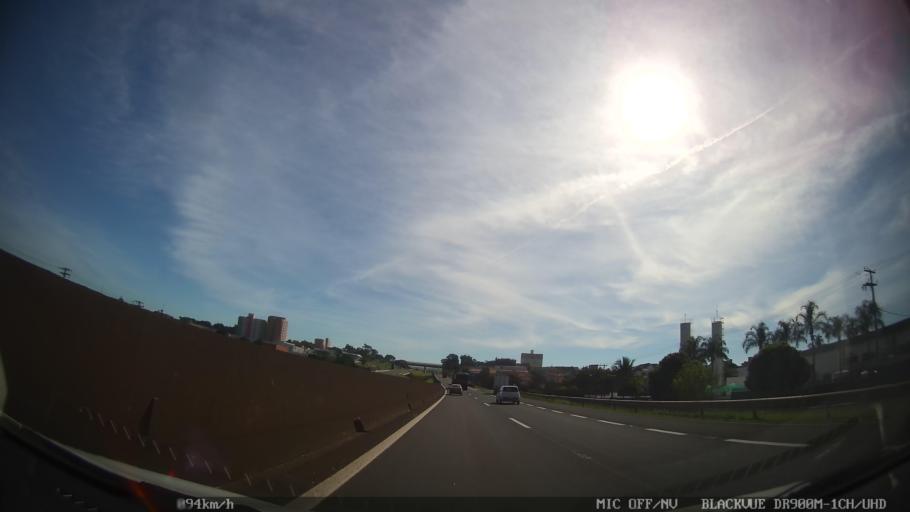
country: BR
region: Sao Paulo
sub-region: Araras
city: Araras
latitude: -22.3616
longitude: -47.3946
